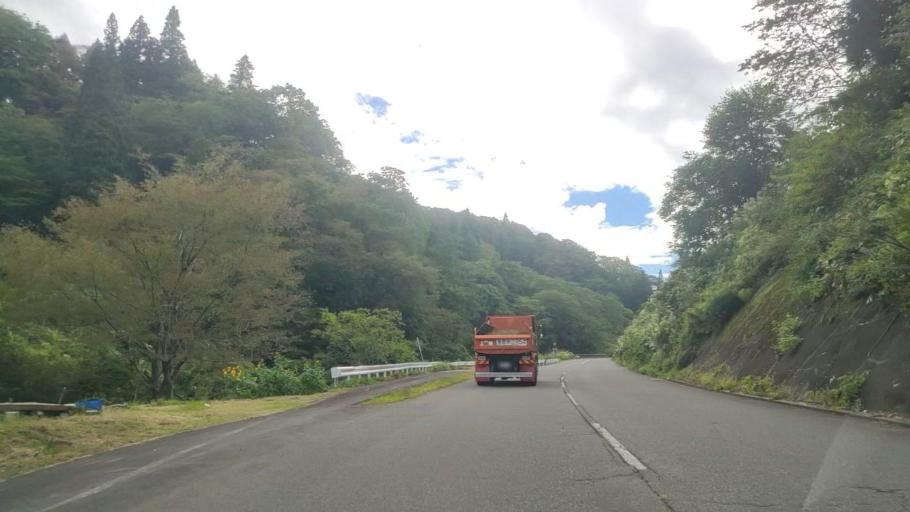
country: JP
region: Nagano
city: Iiyama
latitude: 36.8973
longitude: 138.3202
